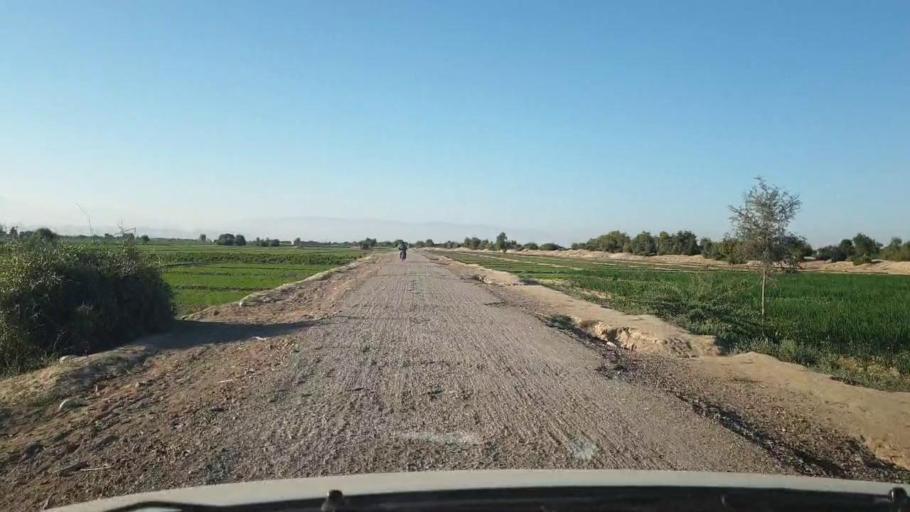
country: PK
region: Sindh
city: Johi
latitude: 26.7626
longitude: 67.4665
